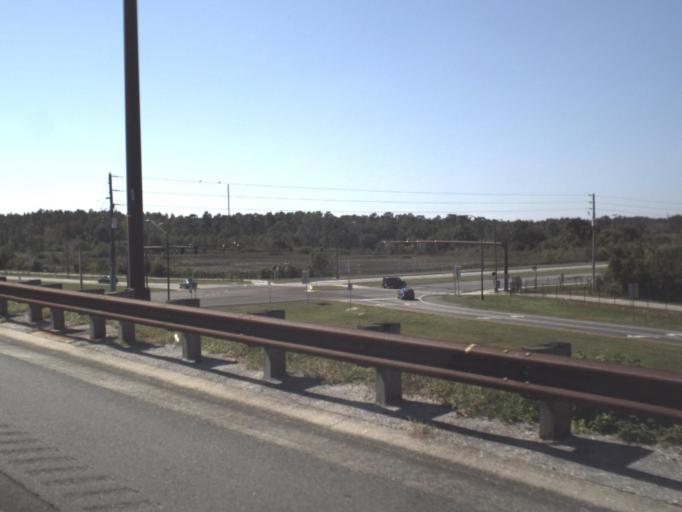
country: US
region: Florida
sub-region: Pasco County
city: Shady Hills
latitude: 28.3318
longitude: -82.5523
